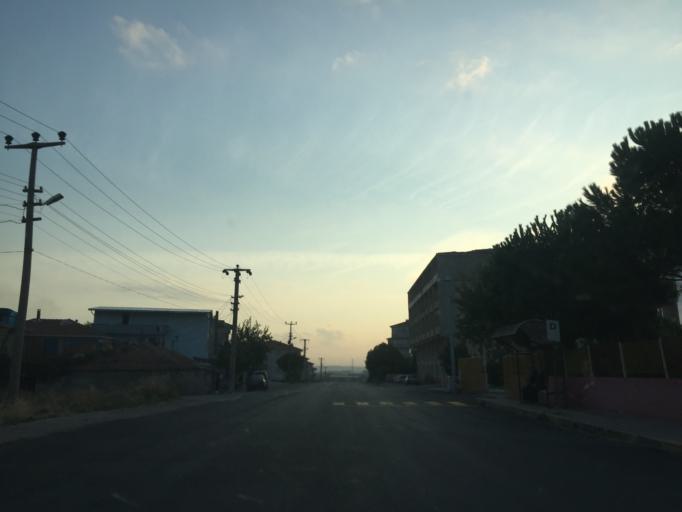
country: TR
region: Balikesir
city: Gonen
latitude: 40.0954
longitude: 27.6599
